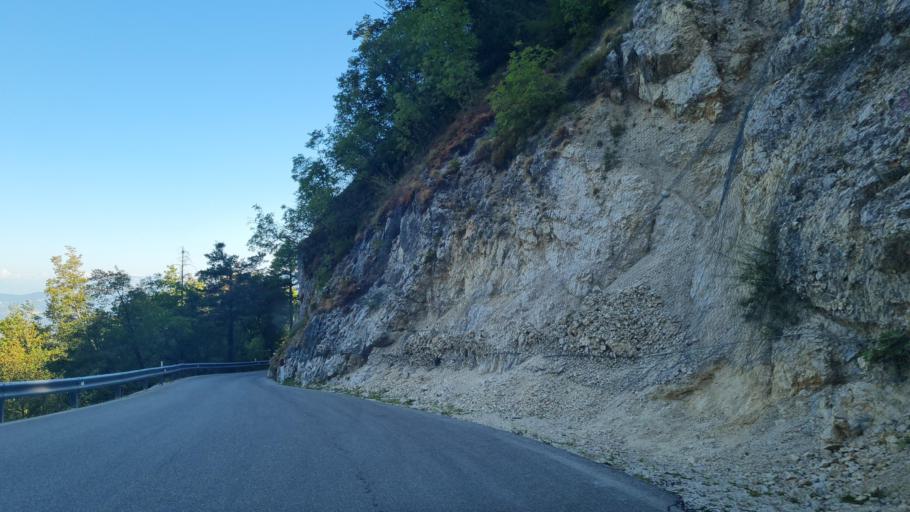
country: IT
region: Trentino-Alto Adige
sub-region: Provincia di Trento
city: Caldonazzo
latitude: 45.9780
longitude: 11.2892
